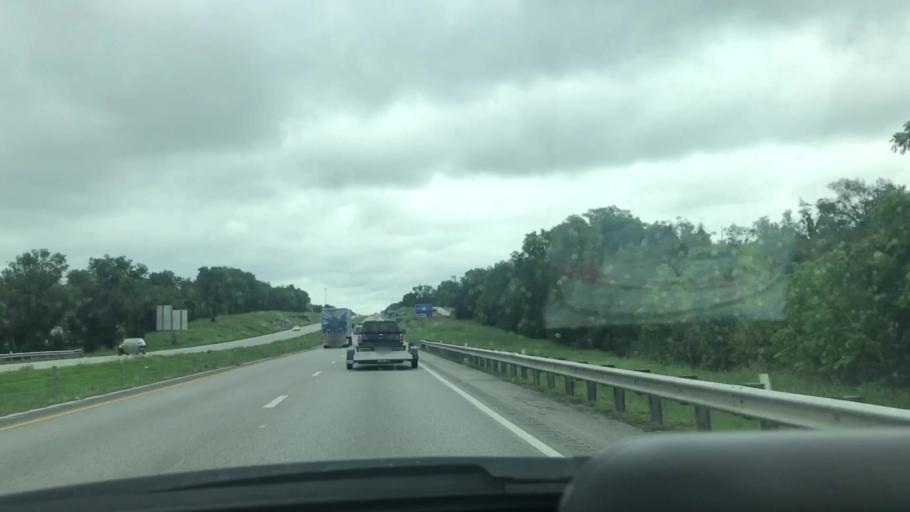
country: US
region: Missouri
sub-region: Greene County
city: Springfield
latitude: 37.2500
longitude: -93.2913
